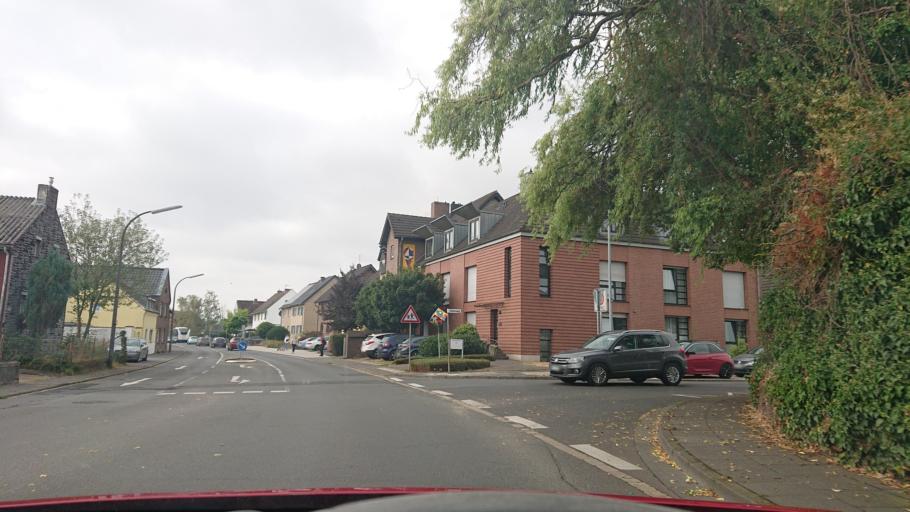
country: DE
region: North Rhine-Westphalia
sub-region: Regierungsbezirk Koln
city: Erftstadt
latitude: 50.8222
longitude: 6.7650
